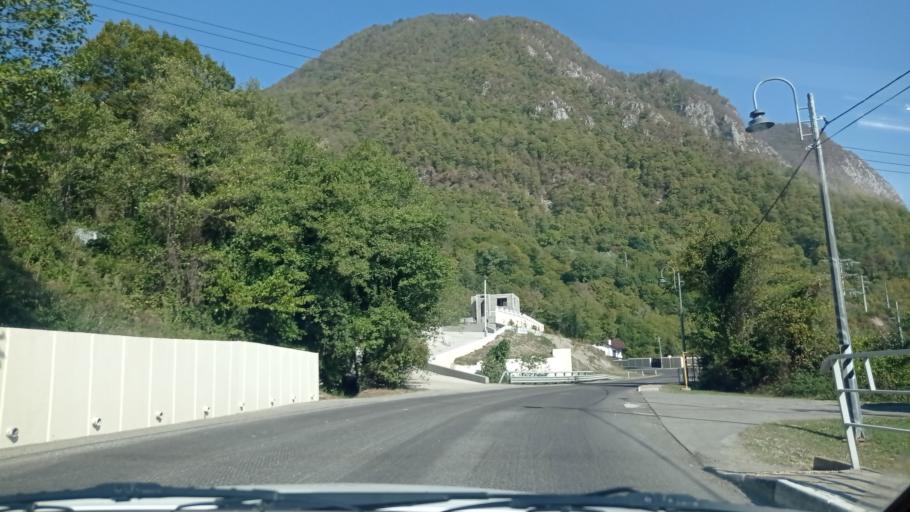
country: RU
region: Krasnodarskiy
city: Vysokoye
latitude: 43.5907
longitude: 40.0071
